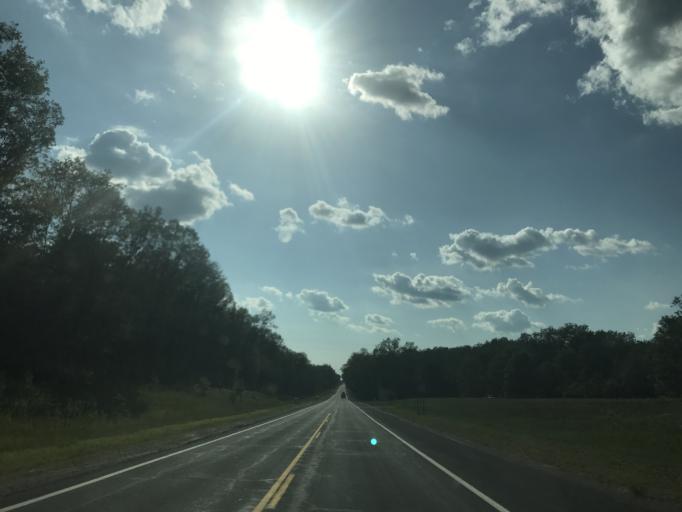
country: US
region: Michigan
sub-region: Newaygo County
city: White Cloud
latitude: 43.5681
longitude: -85.8081
